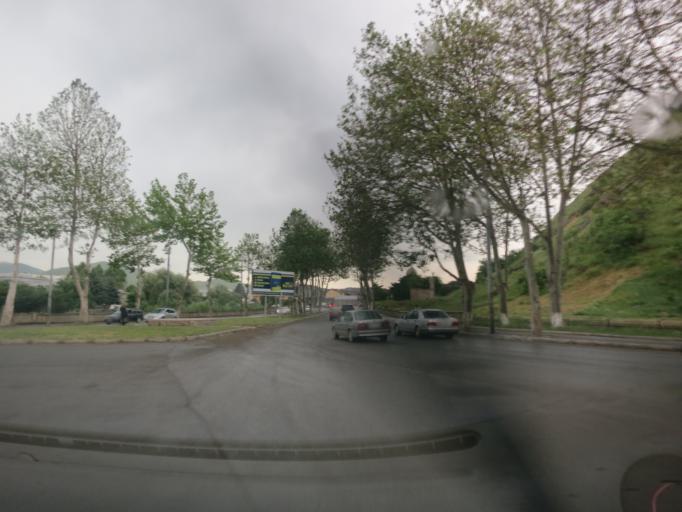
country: GE
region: Shida Kartli
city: Gori
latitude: 41.9875
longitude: 44.1068
